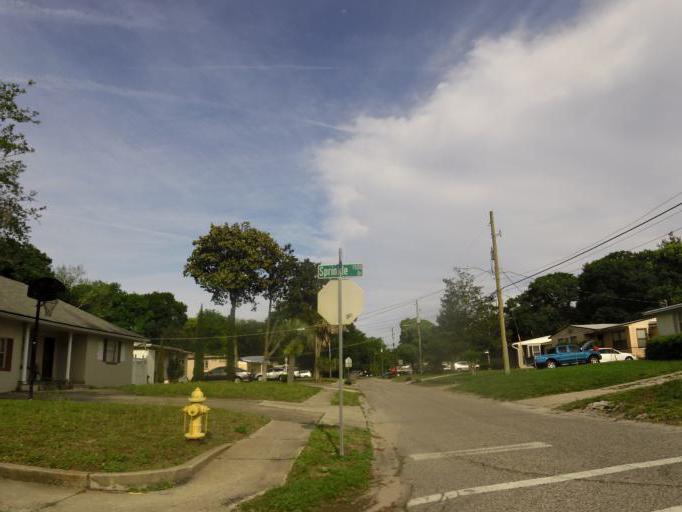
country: US
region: Florida
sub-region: Duval County
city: Jacksonville
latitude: 30.3371
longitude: -81.5923
